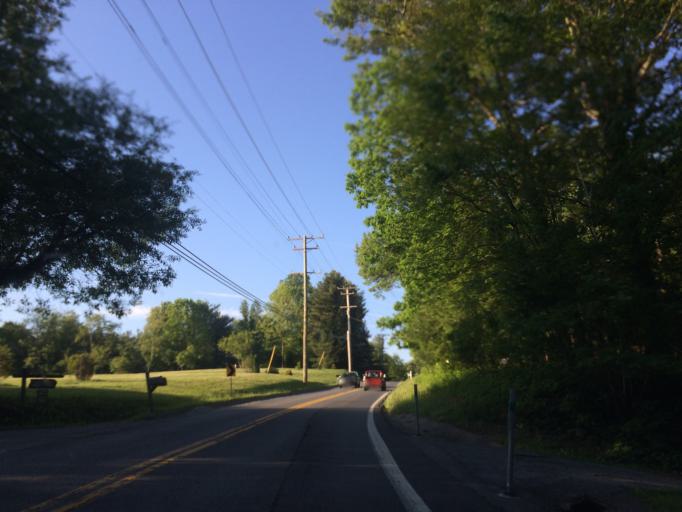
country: US
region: Maryland
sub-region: Carroll County
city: Sykesville
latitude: 39.3717
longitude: -77.0157
